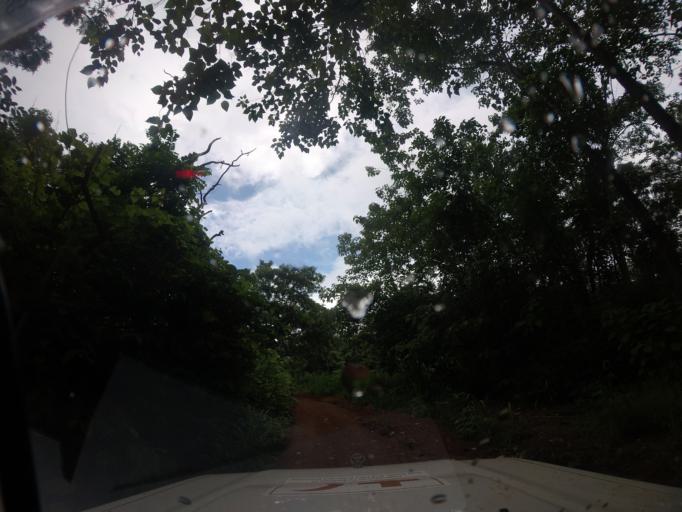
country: SL
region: Northern Province
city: Kamakwie
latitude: 9.7208
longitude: -12.3006
